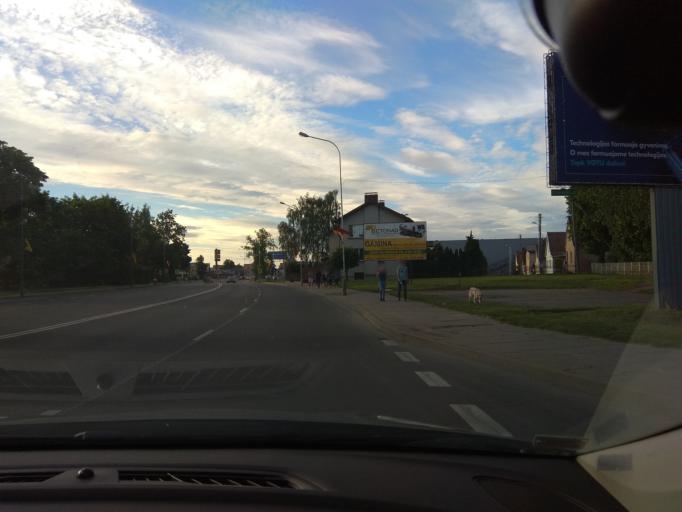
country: LT
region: Marijampoles apskritis
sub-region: Marijampole Municipality
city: Marijampole
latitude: 54.5581
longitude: 23.3546
